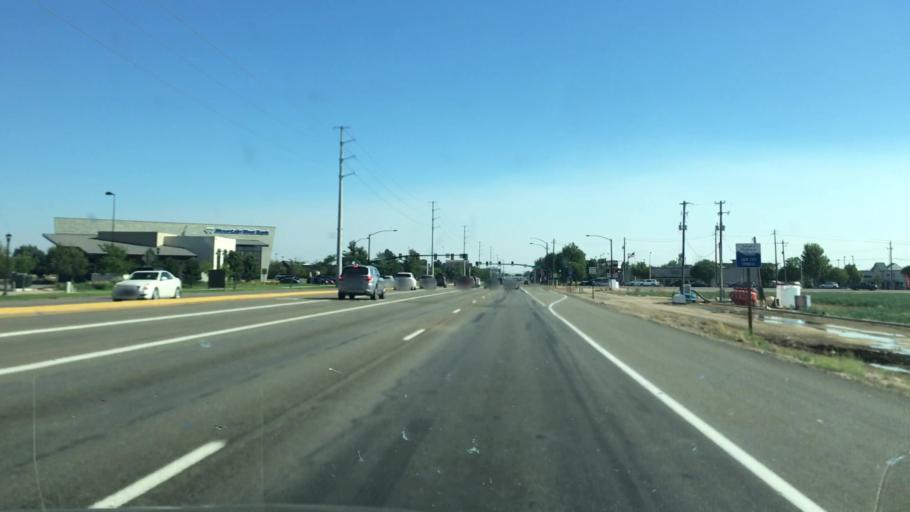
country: US
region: Idaho
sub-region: Ada County
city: Meridian
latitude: 43.6214
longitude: -116.3547
